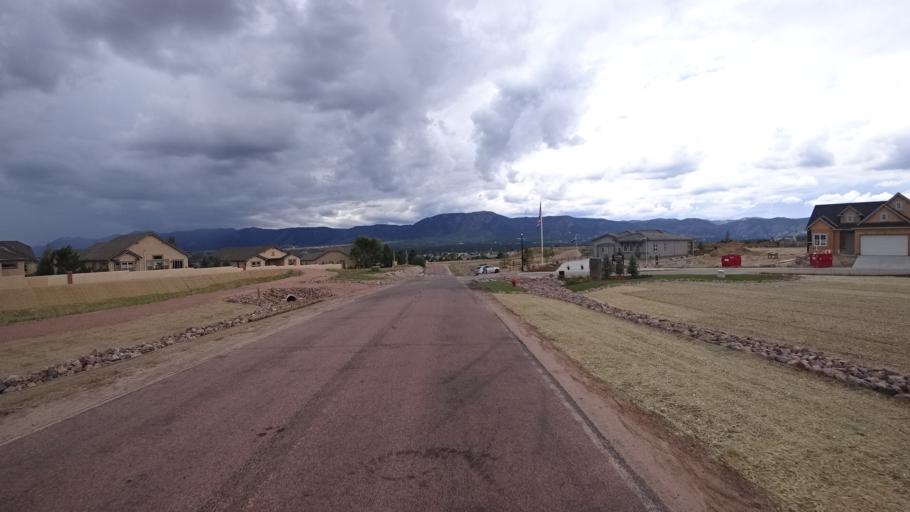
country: US
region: Colorado
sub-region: El Paso County
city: Woodmoor
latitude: 39.0973
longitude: -104.8554
